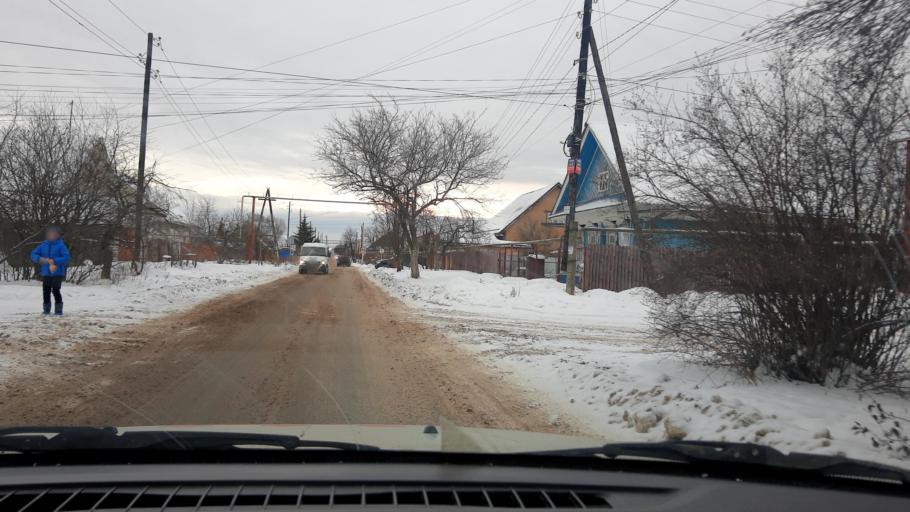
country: RU
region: Nizjnij Novgorod
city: Gorodets
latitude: 56.6650
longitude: 43.4783
